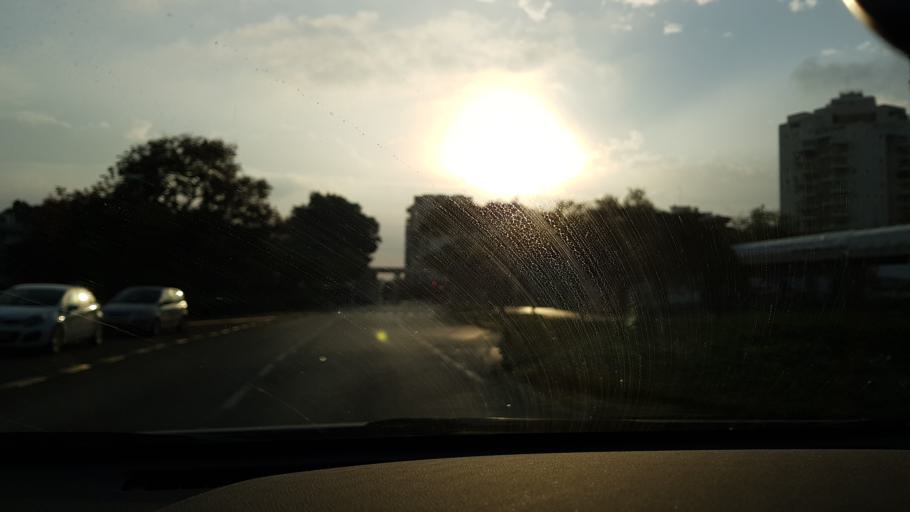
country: IL
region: Central District
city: Ness Ziona
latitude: 31.9046
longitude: 34.8091
